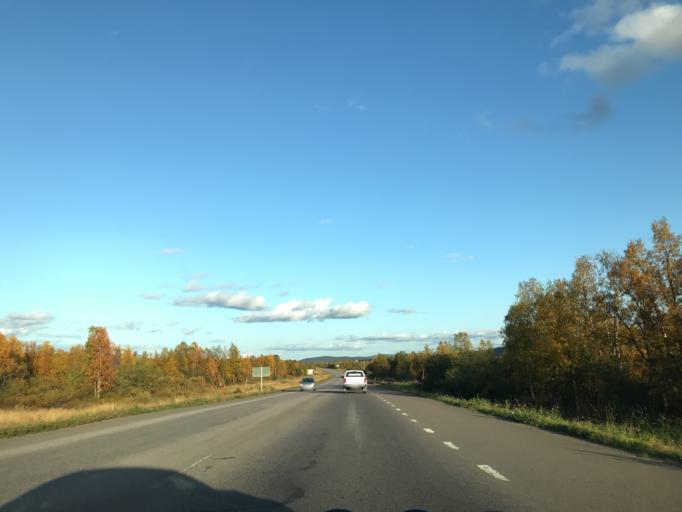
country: SE
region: Norrbotten
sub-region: Kiruna Kommun
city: Kiruna
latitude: 67.8468
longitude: 20.3259
